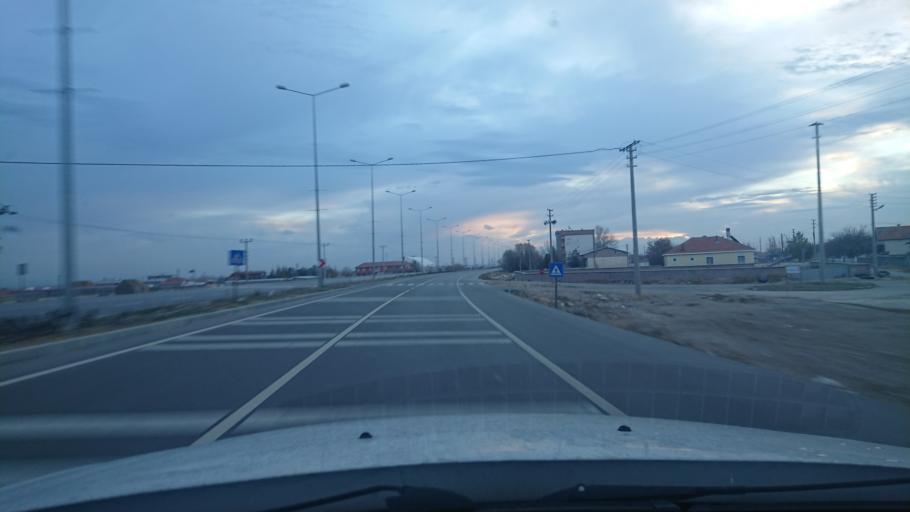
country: TR
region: Aksaray
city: Sultanhani
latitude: 38.2536
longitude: 33.5574
